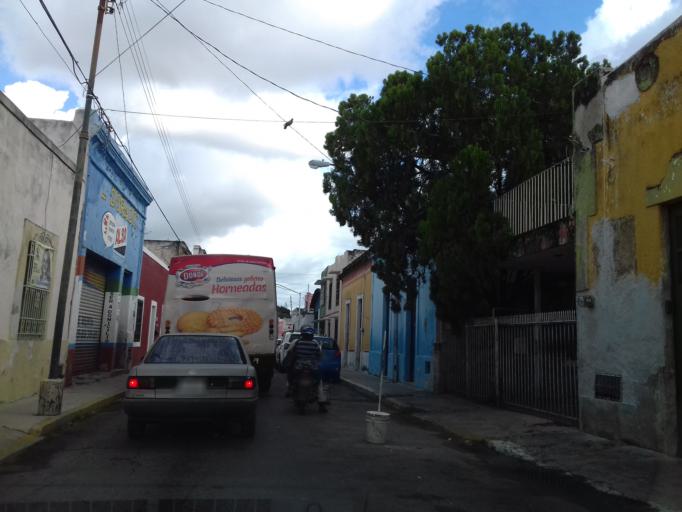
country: MX
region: Yucatan
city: Merida
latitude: 20.9719
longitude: -89.6270
